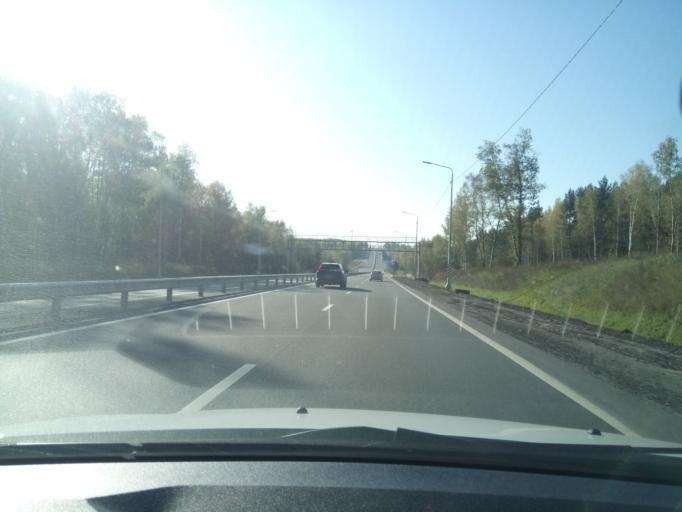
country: RU
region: Nizjnij Novgorod
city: Burevestnik
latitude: 56.0131
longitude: 43.9654
